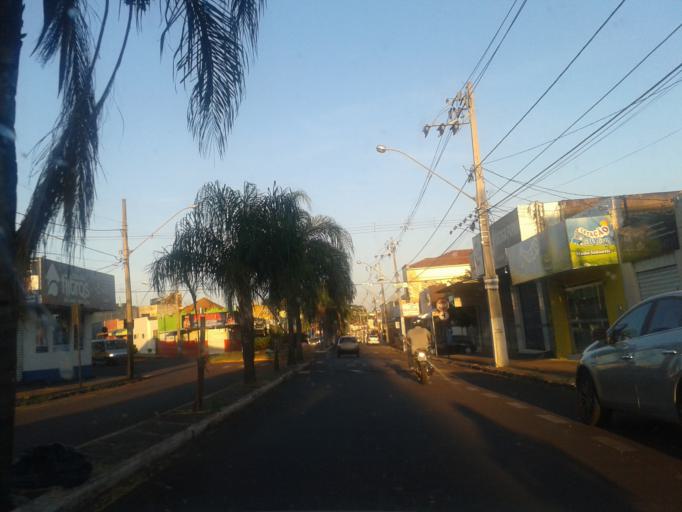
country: BR
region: Minas Gerais
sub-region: Ituiutaba
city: Ituiutaba
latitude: -18.9756
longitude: -49.4653
